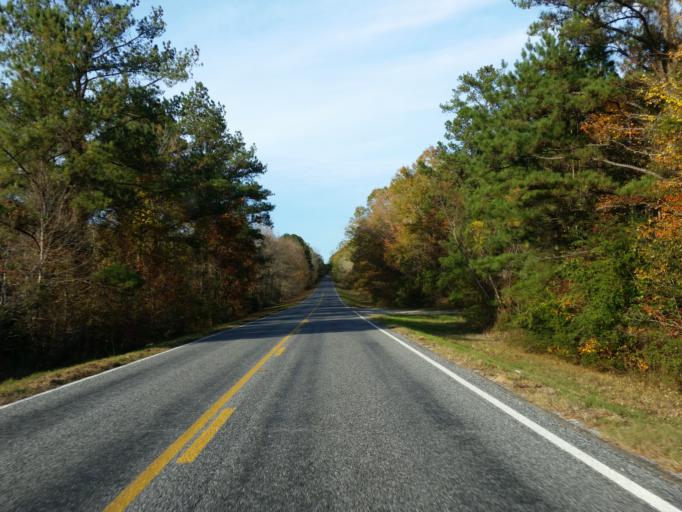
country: US
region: Mississippi
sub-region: Clarke County
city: Quitman
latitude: 31.9635
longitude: -88.9106
